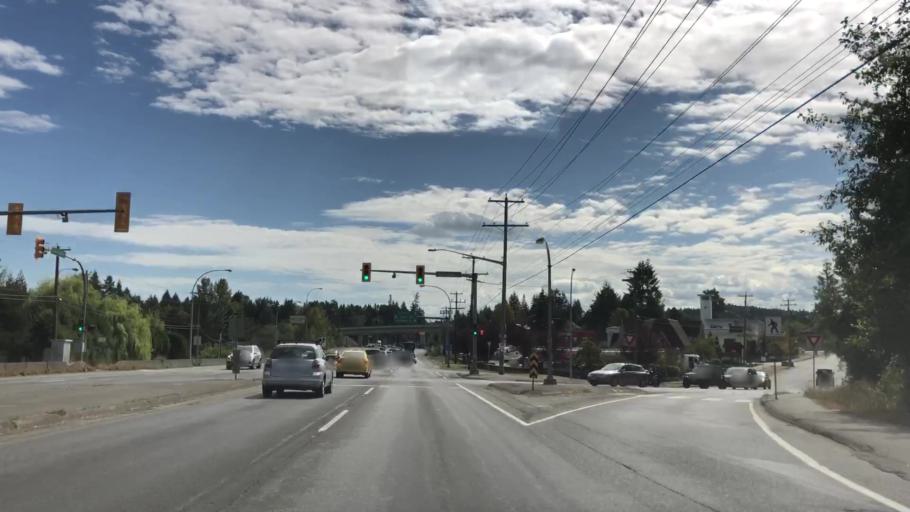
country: CA
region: British Columbia
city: Nanaimo
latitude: 49.1283
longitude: -123.9200
